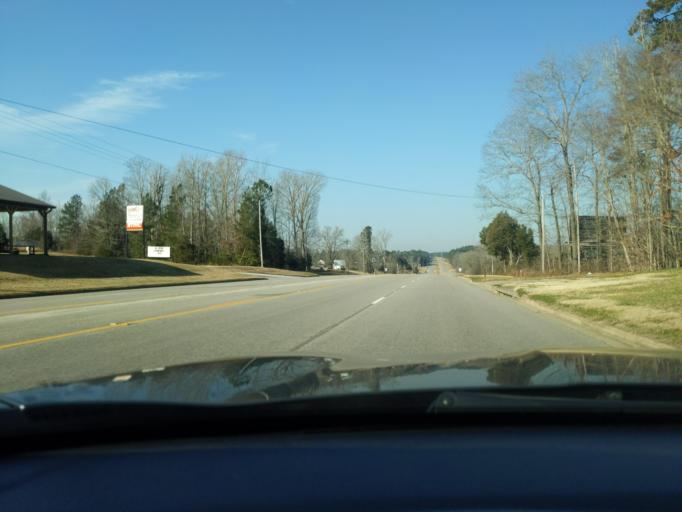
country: US
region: South Carolina
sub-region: Greenwood County
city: Greenwood
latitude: 34.1900
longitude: -82.2494
